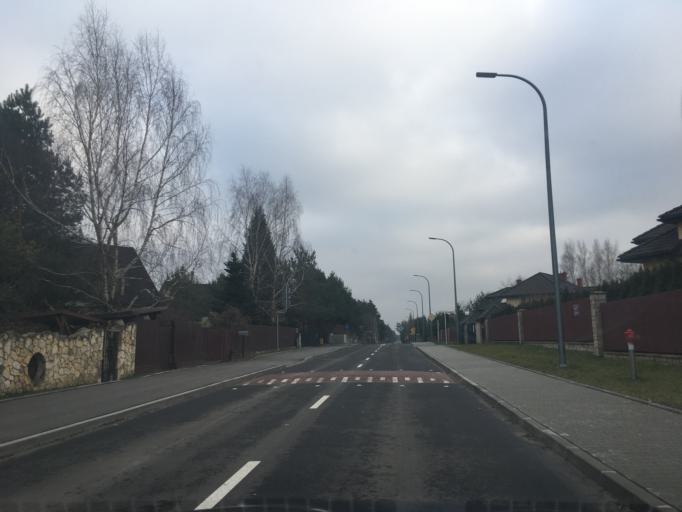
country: PL
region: Masovian Voivodeship
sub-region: Powiat piaseczynski
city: Lesznowola
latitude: 52.0704
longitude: 20.9696
